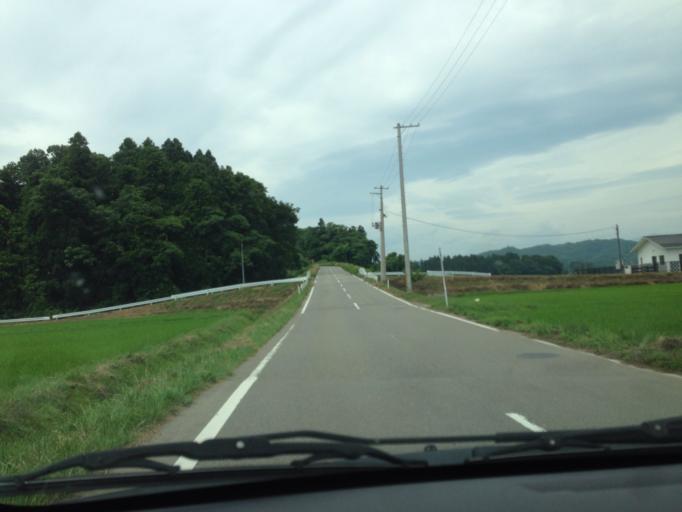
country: JP
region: Fukushima
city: Kitakata
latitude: 37.5904
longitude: 139.8132
